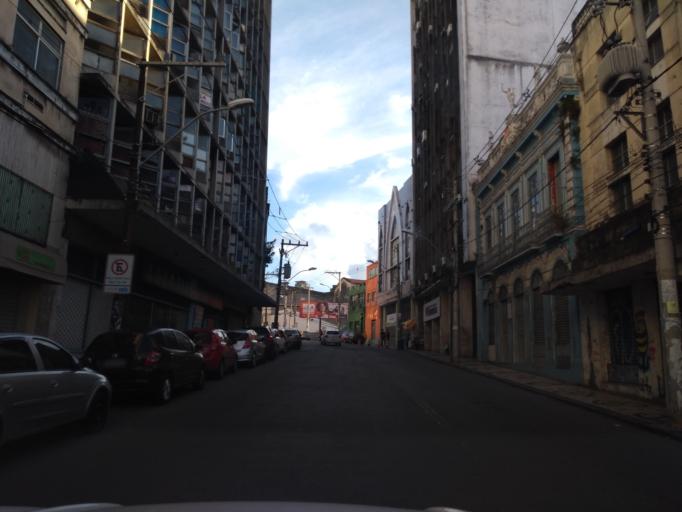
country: BR
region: Bahia
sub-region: Salvador
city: Salvador
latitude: -12.9782
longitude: -38.5149
